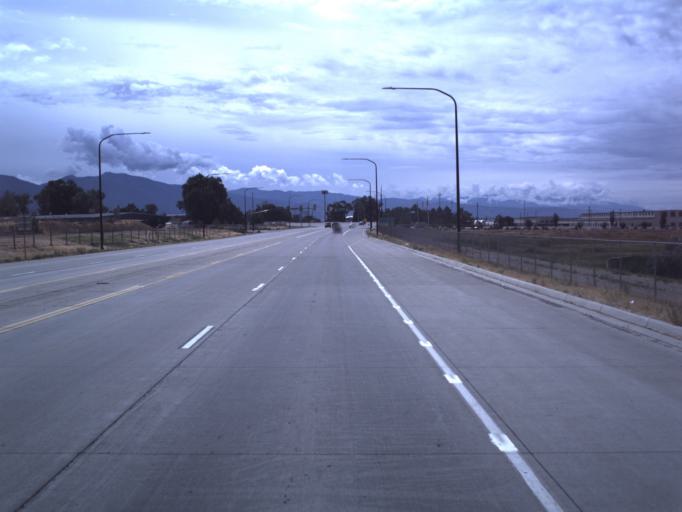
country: US
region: Utah
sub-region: Davis County
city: Clearfield
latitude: 41.1079
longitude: -112.0306
